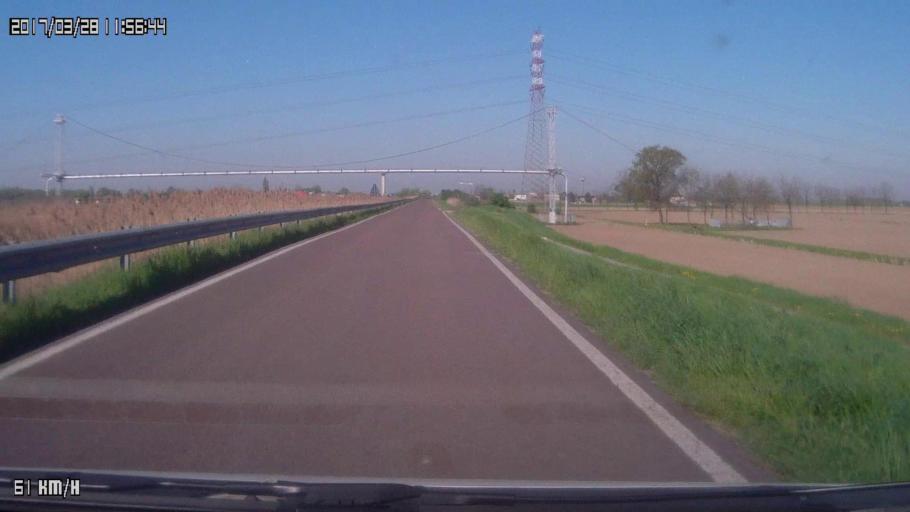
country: IT
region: Veneto
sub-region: Provincia di Venezia
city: Boscochiaro
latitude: 45.1341
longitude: 12.1347
